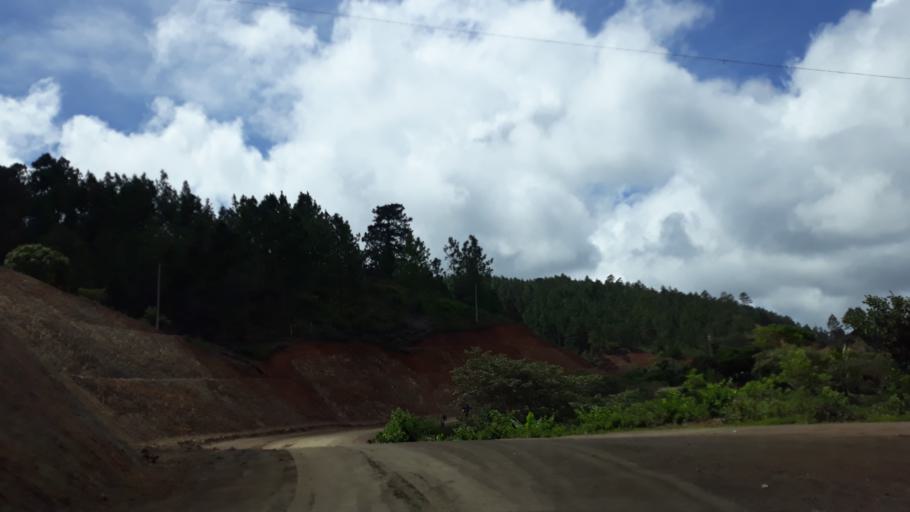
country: HN
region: El Paraiso
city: Santa Cruz
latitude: 13.7660
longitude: -86.6461
